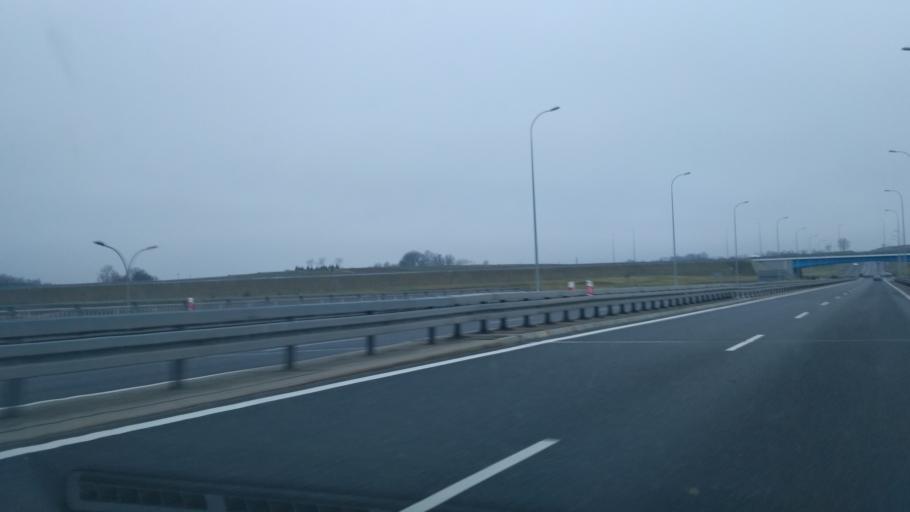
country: PL
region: Subcarpathian Voivodeship
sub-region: Powiat przeworski
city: Mirocin
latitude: 50.0373
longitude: 22.5776
